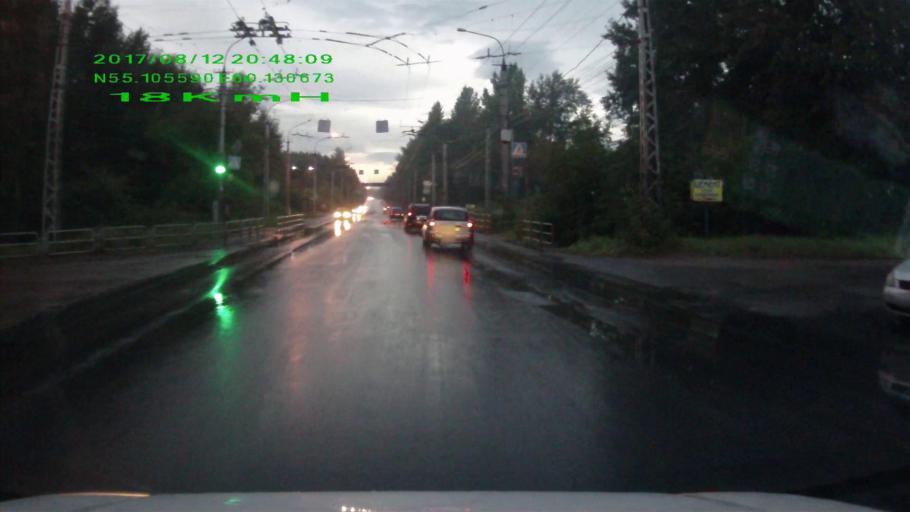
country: RU
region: Chelyabinsk
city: Turgoyak
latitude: 55.1055
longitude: 60.1307
